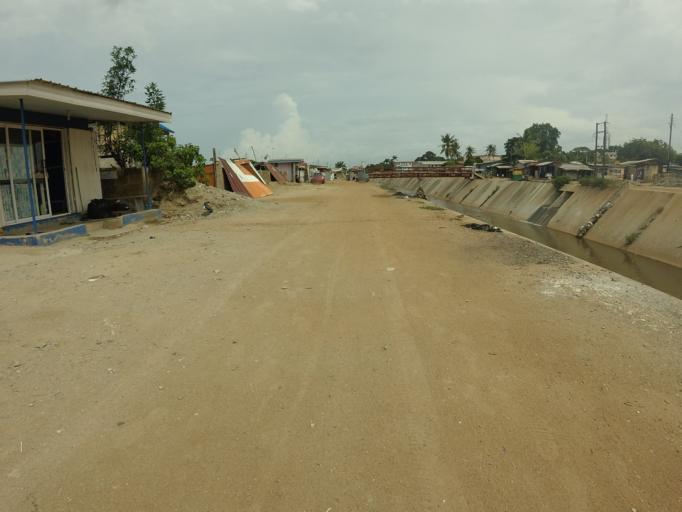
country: GH
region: Greater Accra
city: Accra
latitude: 5.5999
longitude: -0.2211
